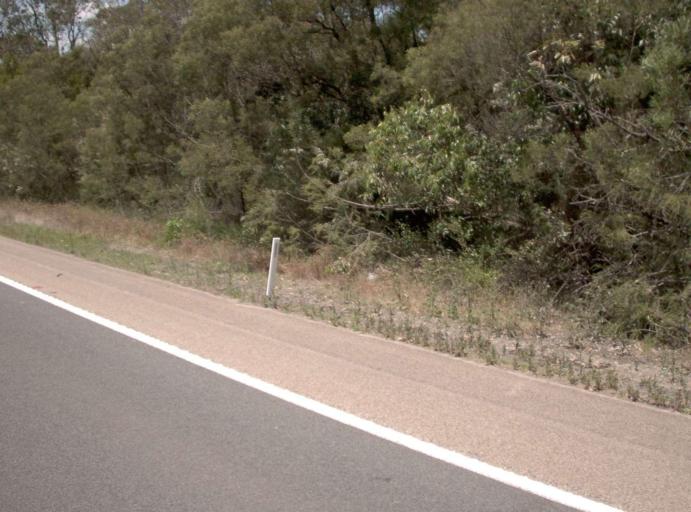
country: AU
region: Victoria
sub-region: East Gippsland
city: Lakes Entrance
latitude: -37.7023
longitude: 148.5580
